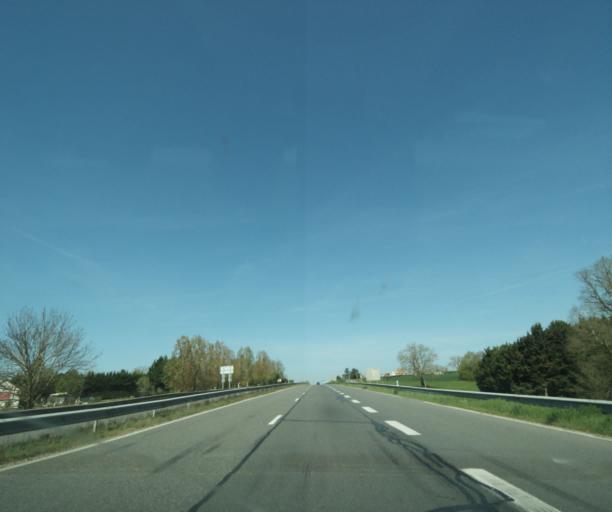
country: FR
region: Bourgogne
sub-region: Departement de la Nievre
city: Saint-Pierre-le-Moutier
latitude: 46.7946
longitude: 3.1229
